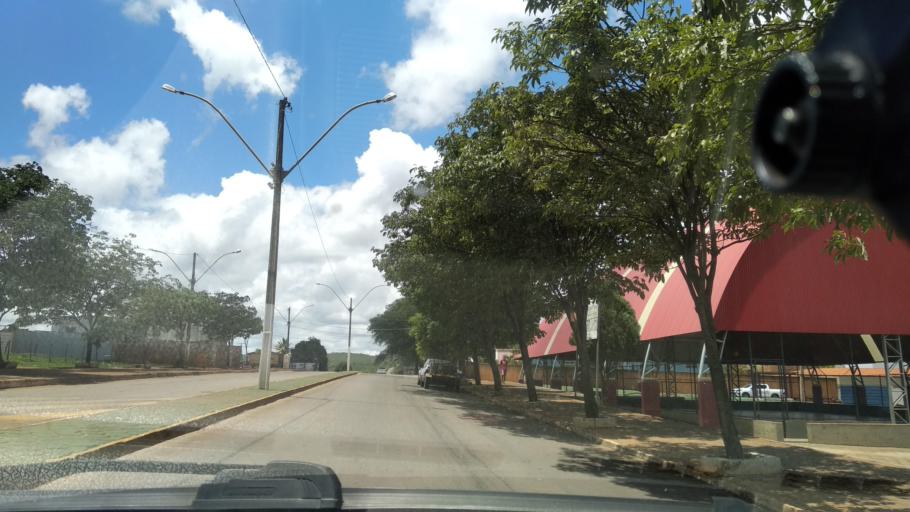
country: BR
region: Bahia
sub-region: Caetite
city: Caetite
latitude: -14.0546
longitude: -42.4842
